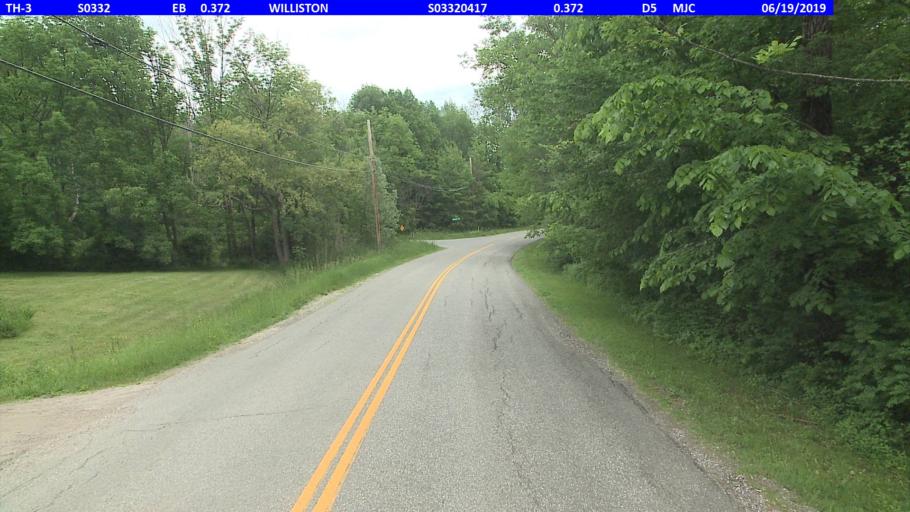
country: US
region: Vermont
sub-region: Chittenden County
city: Williston
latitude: 44.4258
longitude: -73.1146
